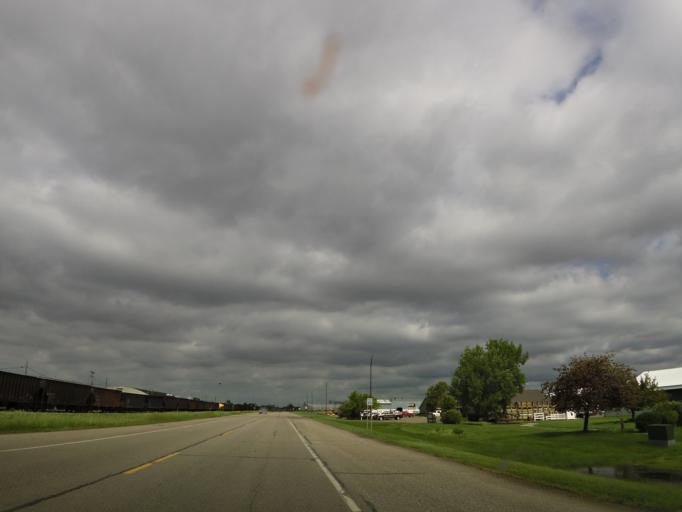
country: US
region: Minnesota
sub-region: Polk County
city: East Grand Forks
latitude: 47.9181
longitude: -96.9889
